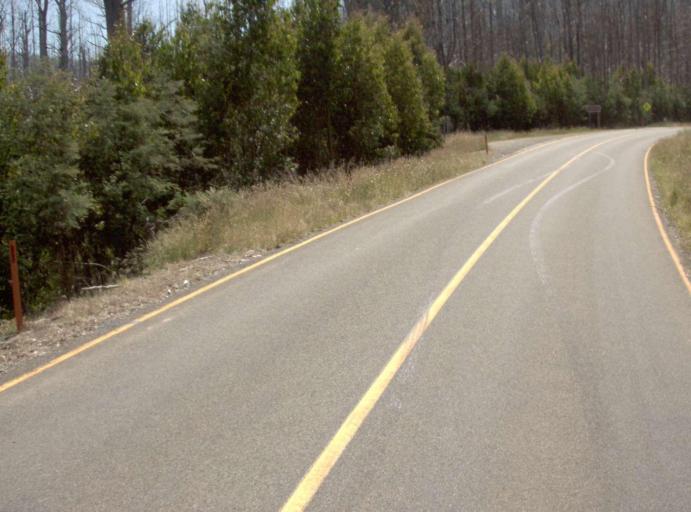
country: AU
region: Victoria
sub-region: Yarra Ranges
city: Millgrove
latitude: -37.5608
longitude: 145.8859
